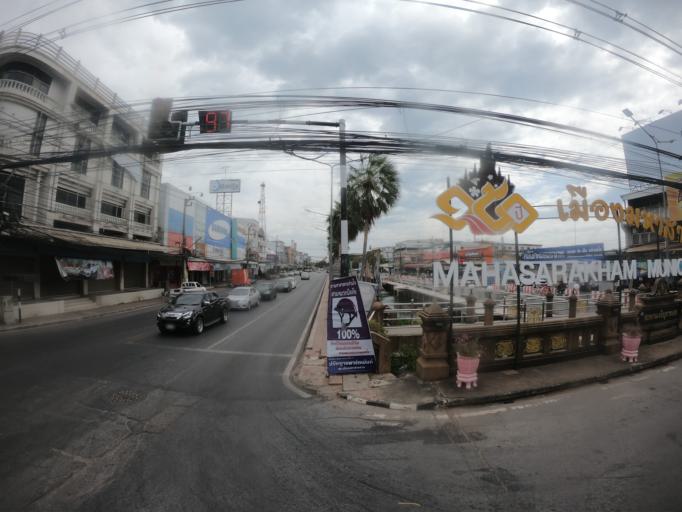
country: TH
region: Maha Sarakham
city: Maha Sarakham
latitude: 16.1821
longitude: 103.3005
